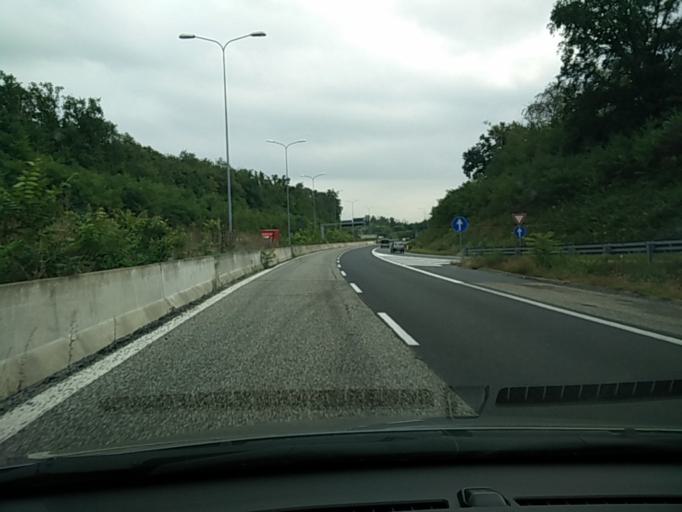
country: IT
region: Lombardy
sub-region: Provincia di Varese
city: Lonate Pozzolo
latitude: 45.5832
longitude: 8.7271
